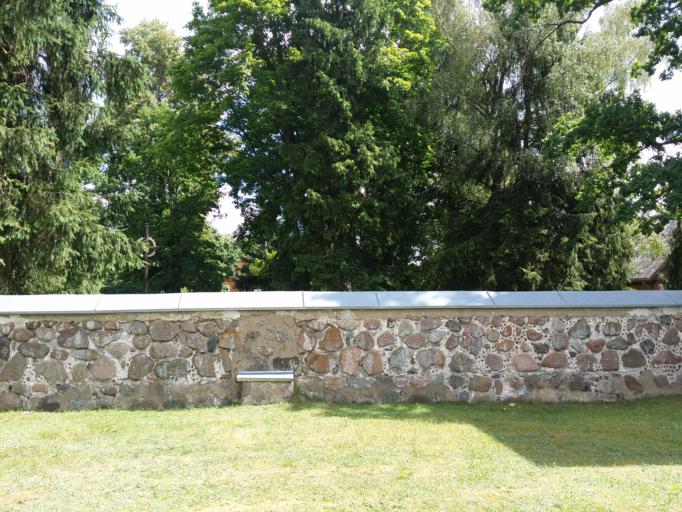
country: LT
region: Vilnius County
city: Elektrenai
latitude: 54.9548
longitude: 24.6536
